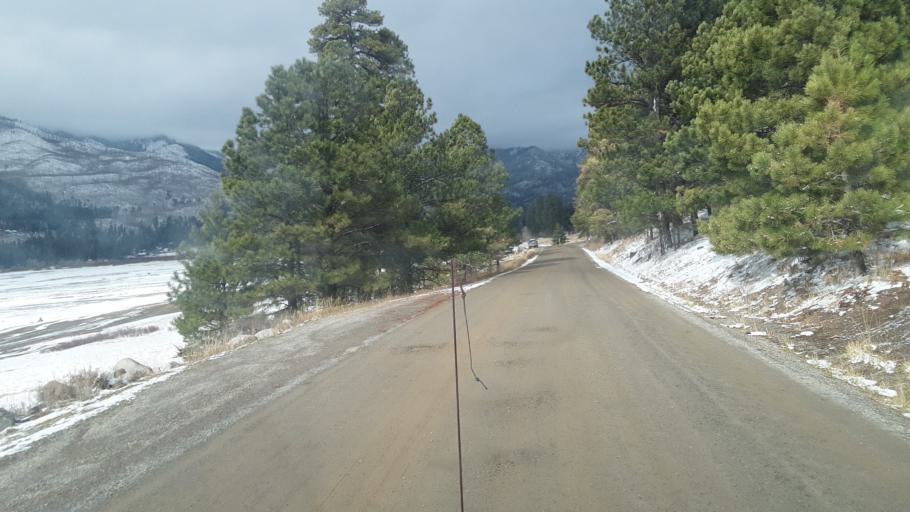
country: US
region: Colorado
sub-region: La Plata County
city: Bayfield
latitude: 37.4279
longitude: -107.5395
